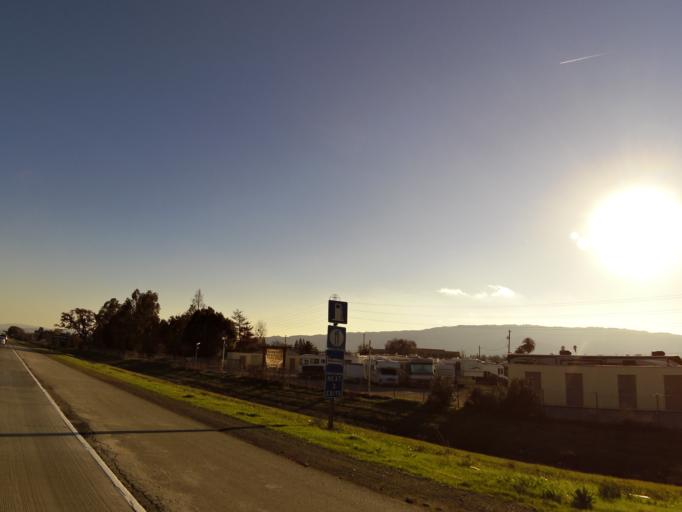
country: US
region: California
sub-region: Santa Clara County
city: Gilroy
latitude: 37.0341
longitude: -121.5733
